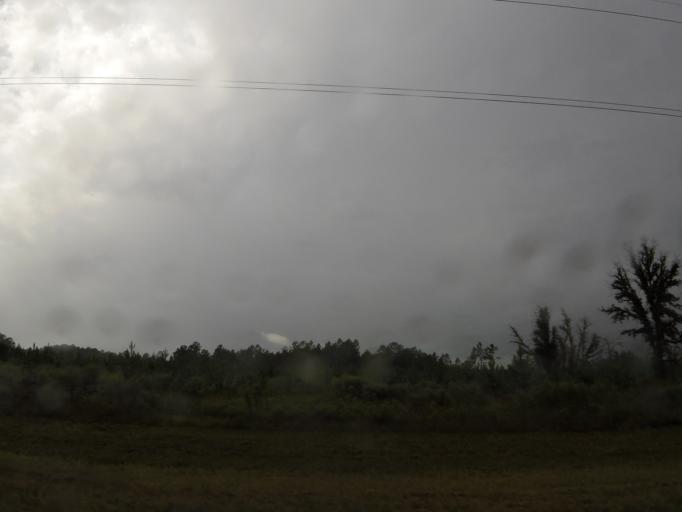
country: US
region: Florida
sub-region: Baker County
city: Macclenny
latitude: 30.3991
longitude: -82.1185
